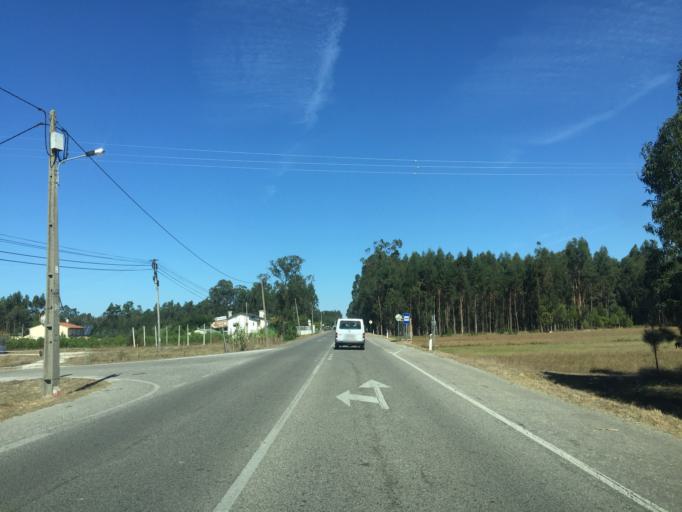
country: PT
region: Coimbra
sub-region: Figueira da Foz
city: Alhadas
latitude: 40.2862
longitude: -8.7684
